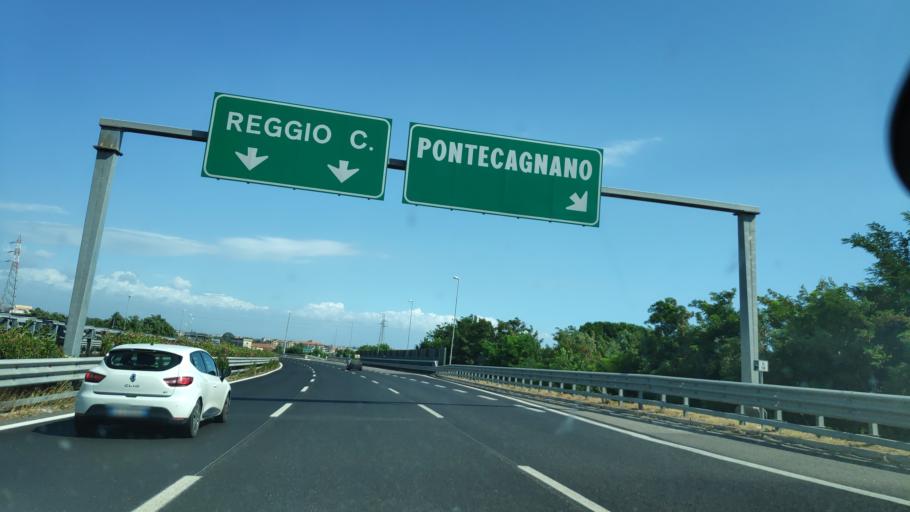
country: IT
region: Campania
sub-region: Provincia di Salerno
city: Pontecagnano
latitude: 40.6567
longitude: 14.8633
